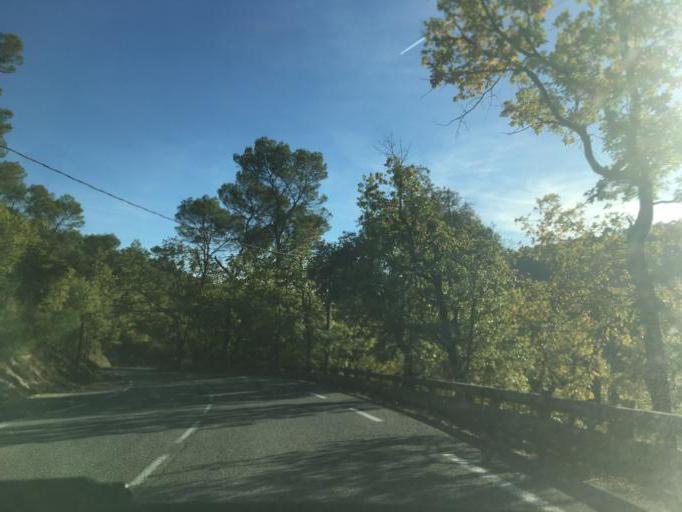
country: FR
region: Provence-Alpes-Cote d'Azur
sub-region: Departement du Var
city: Callas
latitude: 43.5580
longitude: 6.5699
